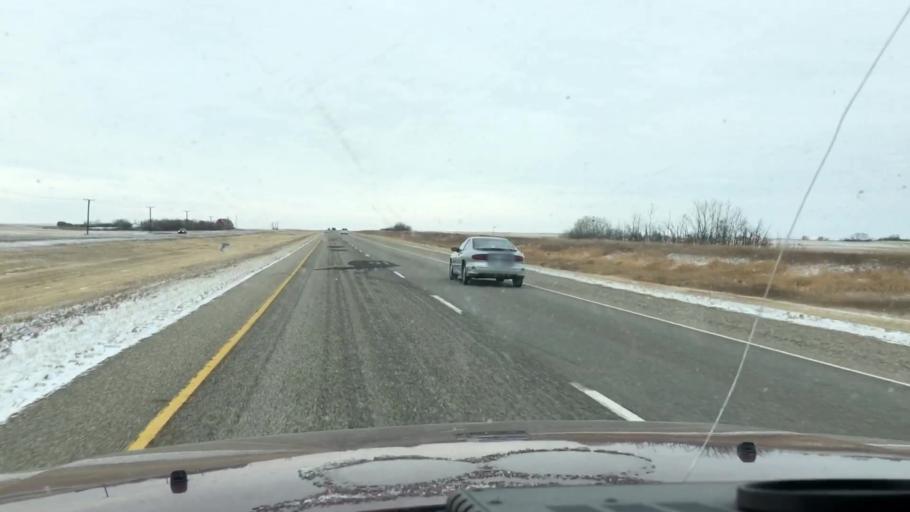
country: CA
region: Saskatchewan
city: Watrous
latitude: 51.4249
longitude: -106.1963
